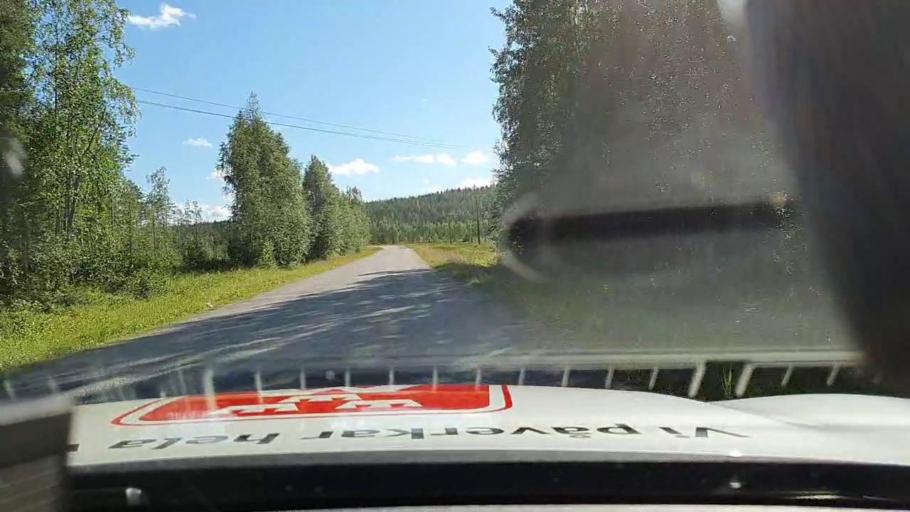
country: SE
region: Norrbotten
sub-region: Overkalix Kommun
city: OEverkalix
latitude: 66.2473
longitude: 23.0062
